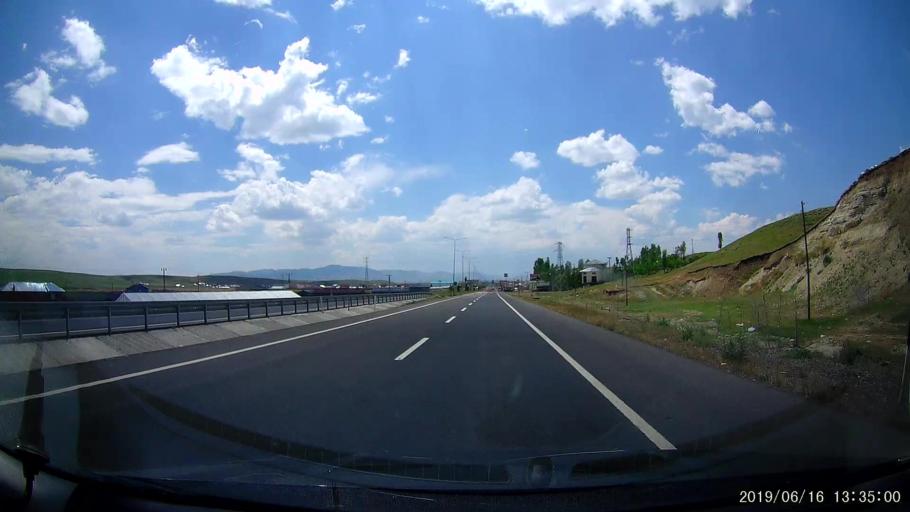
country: TR
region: Agri
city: Agri
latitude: 39.7129
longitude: 43.1143
